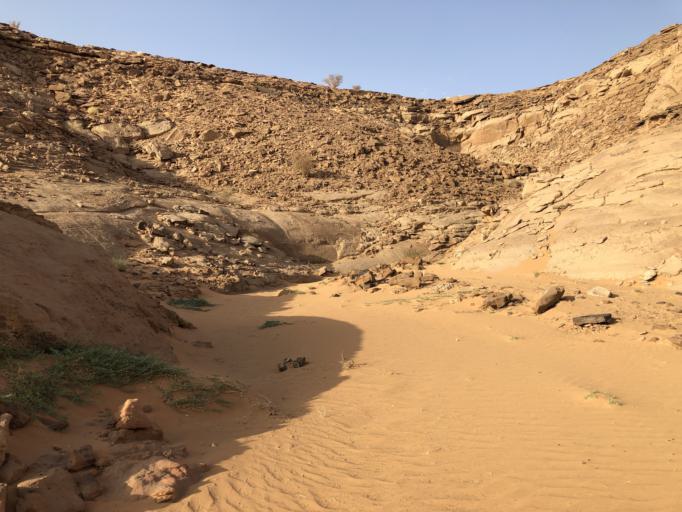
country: SA
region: Ar Riyad
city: shokhaib
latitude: 23.6088
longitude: 46.0781
